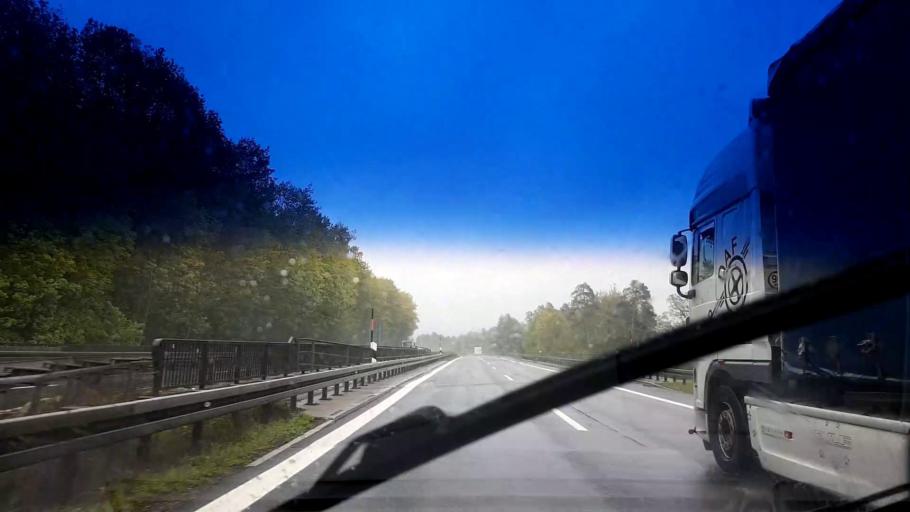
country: DE
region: Bavaria
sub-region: Upper Franconia
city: Eckersdorf
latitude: 50.0241
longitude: 11.4276
